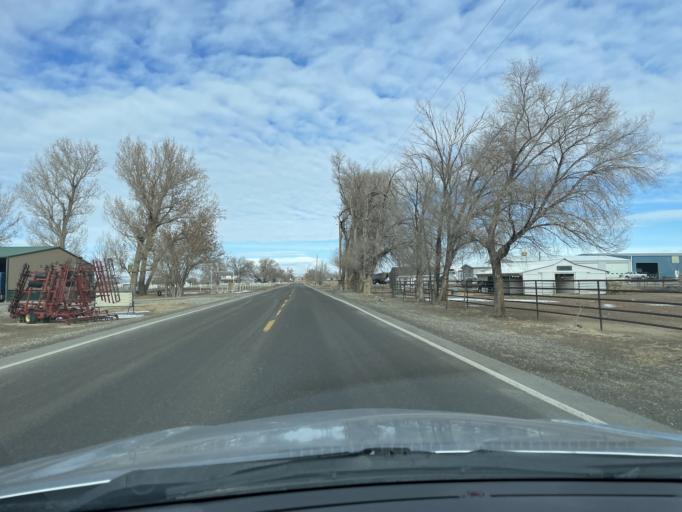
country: US
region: Colorado
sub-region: Mesa County
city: Loma
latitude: 39.2469
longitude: -108.8129
